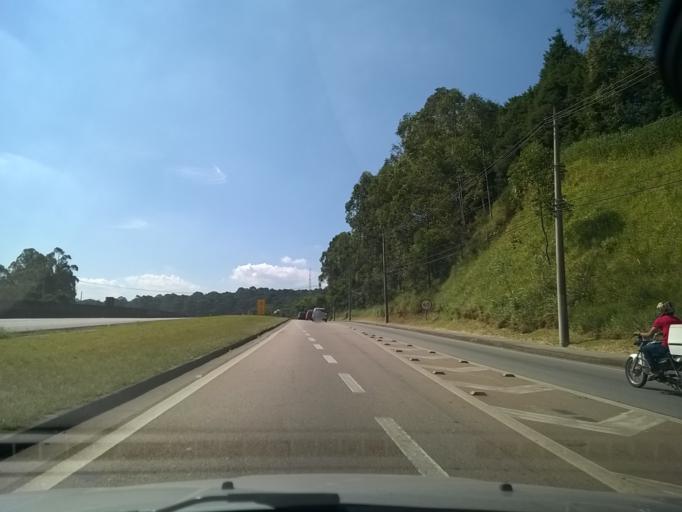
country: BR
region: Sao Paulo
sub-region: Caieiras
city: Caieiras
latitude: -23.4267
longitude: -46.7873
